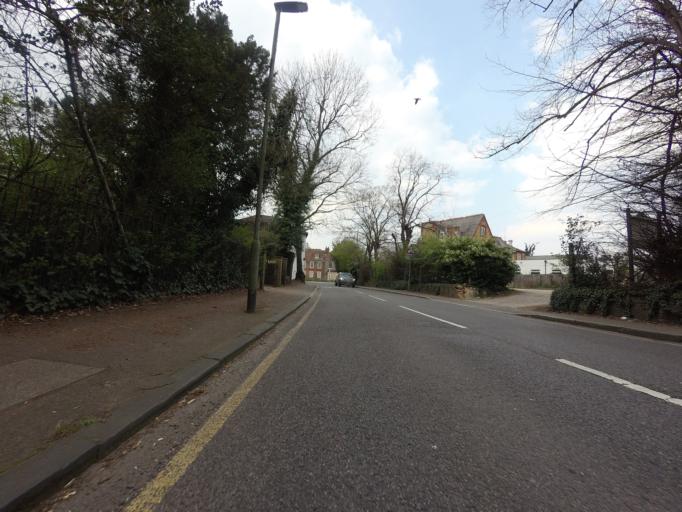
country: GB
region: England
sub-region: Greater London
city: Orpington
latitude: 51.3856
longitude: 0.1138
